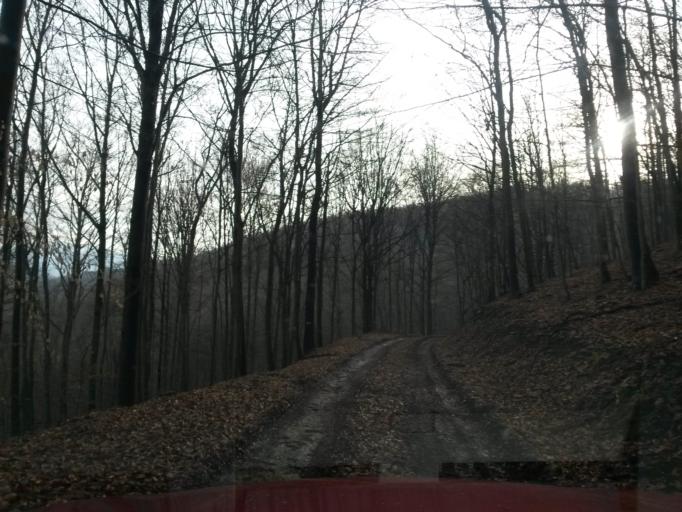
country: SK
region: Kosicky
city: Dobsina
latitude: 48.7467
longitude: 20.4031
